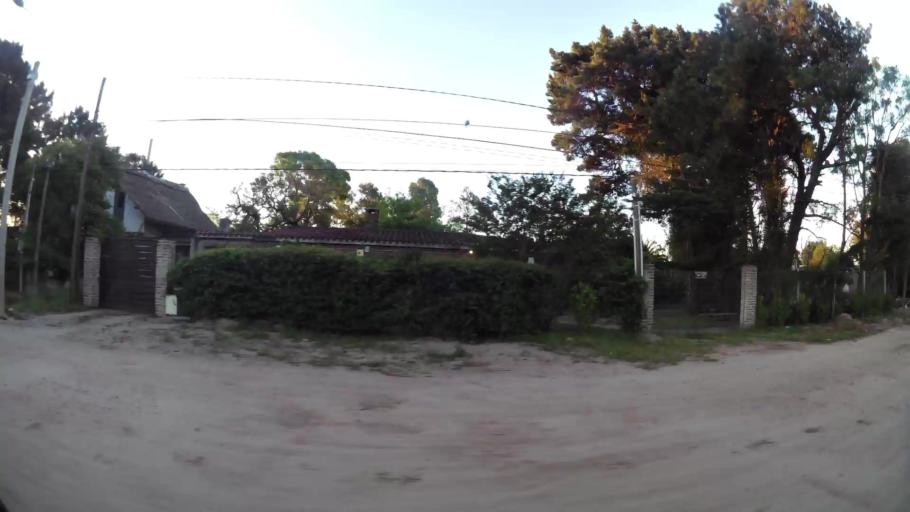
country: UY
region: Canelones
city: Barra de Carrasco
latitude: -34.8428
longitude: -55.9913
